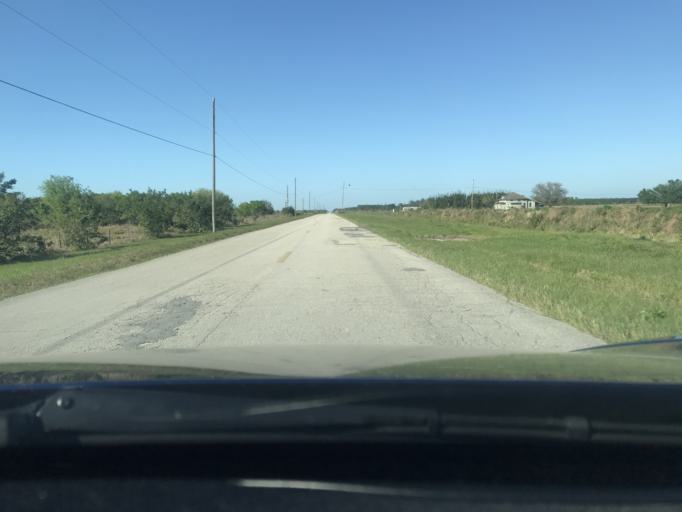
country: US
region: Florida
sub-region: Saint Lucie County
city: Fort Pierce South
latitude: 27.3869
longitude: -80.4975
